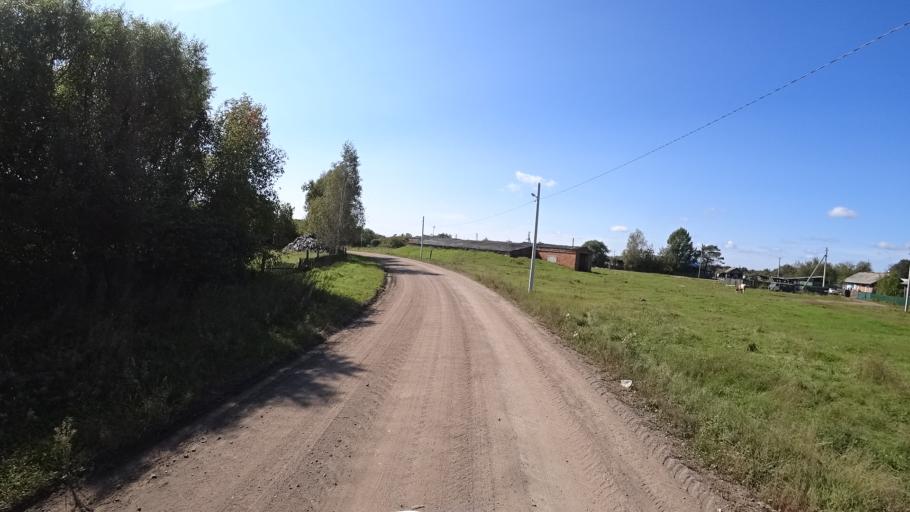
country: RU
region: Amur
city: Arkhara
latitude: 49.4045
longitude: 130.1539
